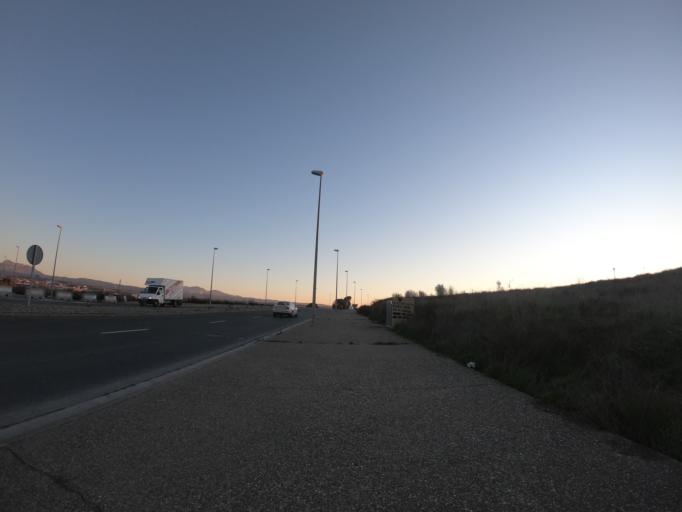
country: ES
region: Basque Country
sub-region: Provincia de Alava
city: Oyon
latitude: 42.4862
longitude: -2.4327
